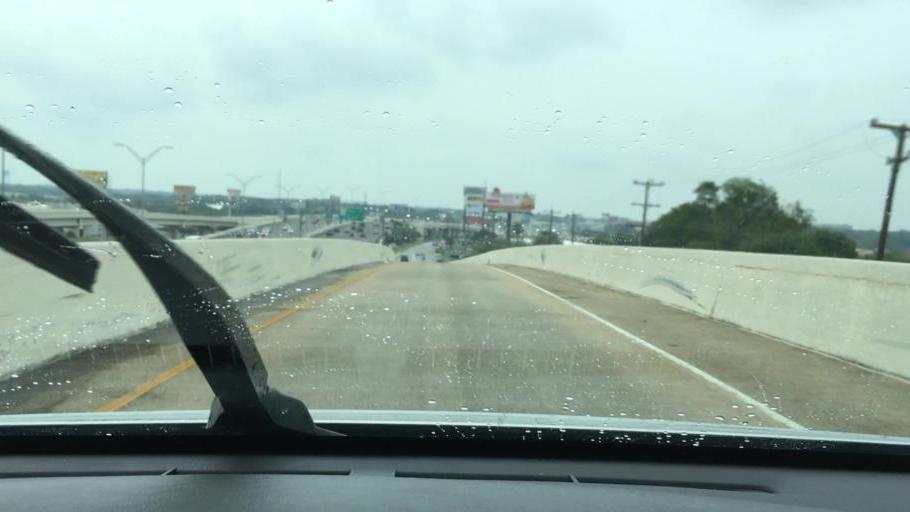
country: US
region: Texas
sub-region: Bexar County
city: Castle Hills
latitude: 29.5130
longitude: -98.5324
